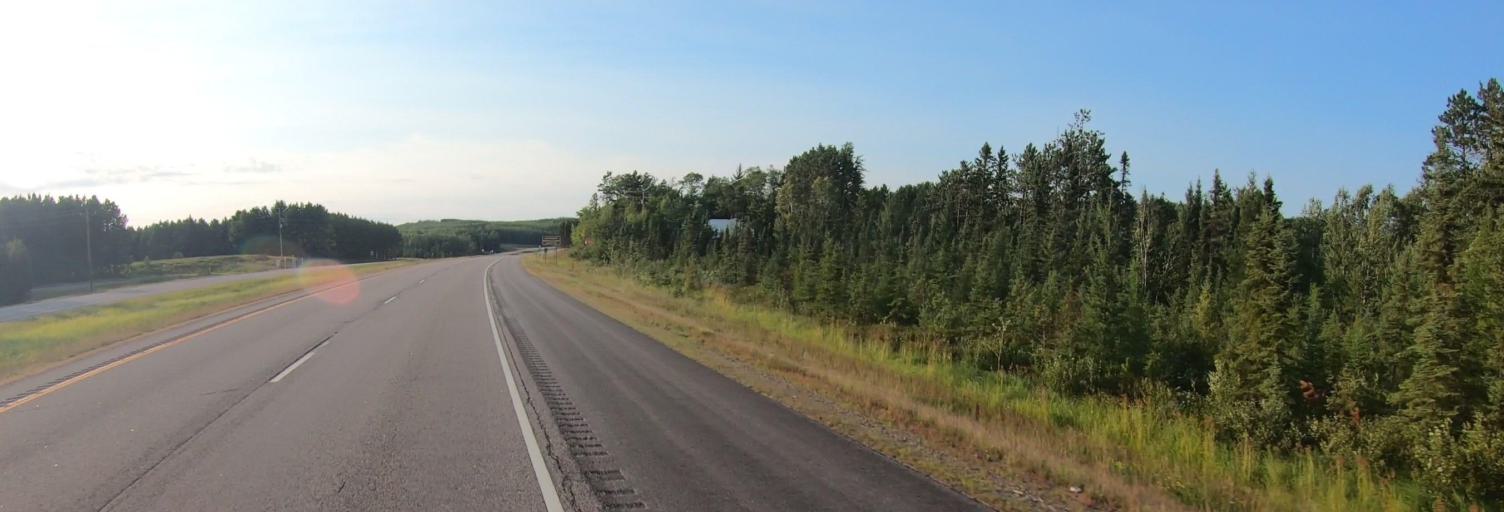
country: US
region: Minnesota
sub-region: Saint Louis County
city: Mountain Iron
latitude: 47.6745
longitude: -92.6336
